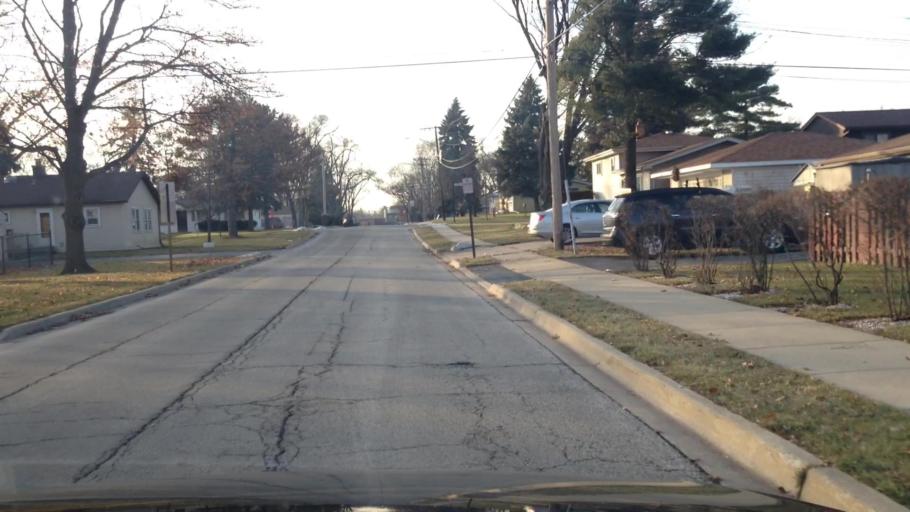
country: US
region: Illinois
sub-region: DuPage County
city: Wood Dale
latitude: 41.9670
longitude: -87.9750
